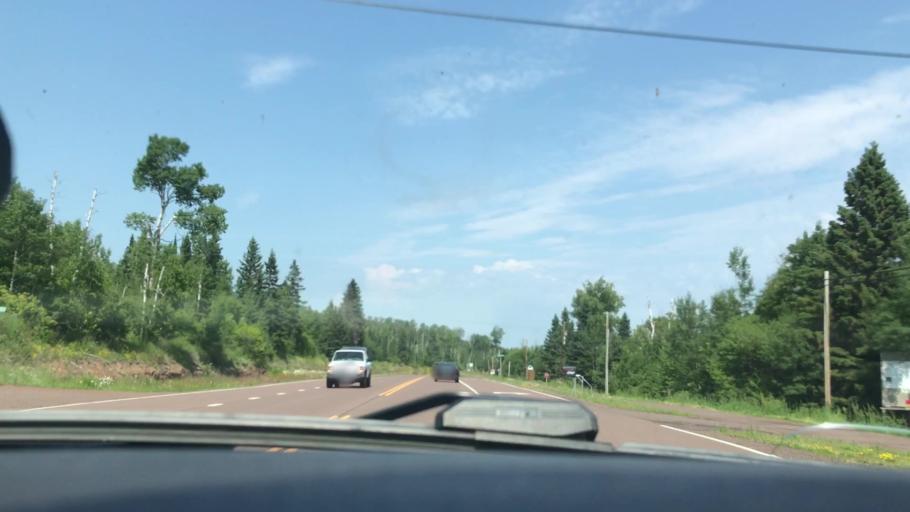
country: US
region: Minnesota
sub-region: Cook County
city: Grand Marais
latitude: 47.6042
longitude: -90.7815
